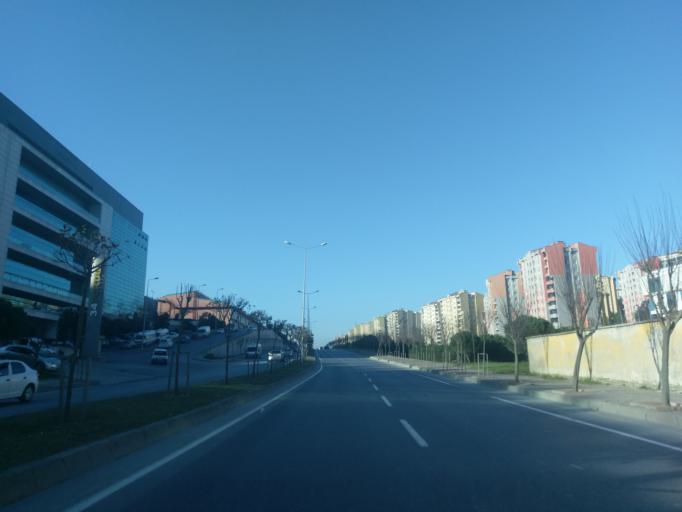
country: TR
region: Istanbul
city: Basaksehir
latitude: 41.0941
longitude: 28.8021
